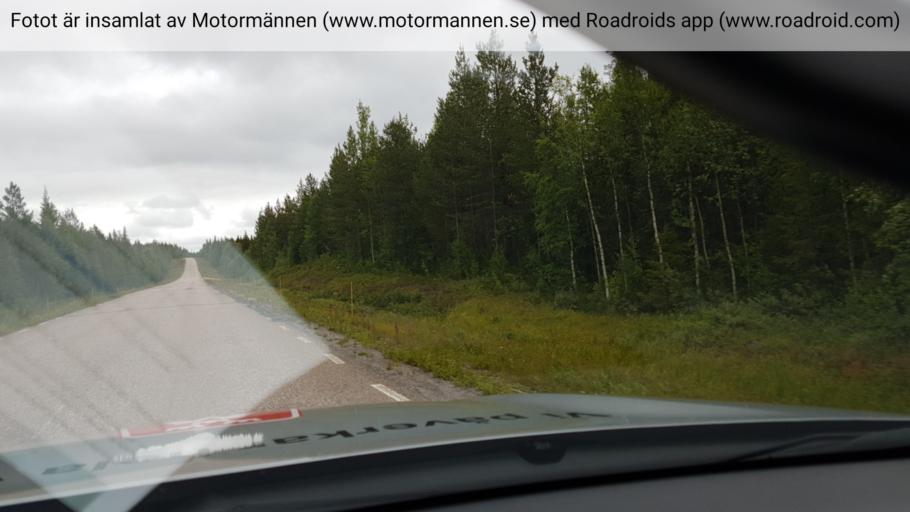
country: SE
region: Norrbotten
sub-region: Overkalix Kommun
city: OEverkalix
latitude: 67.0366
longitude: 22.0290
